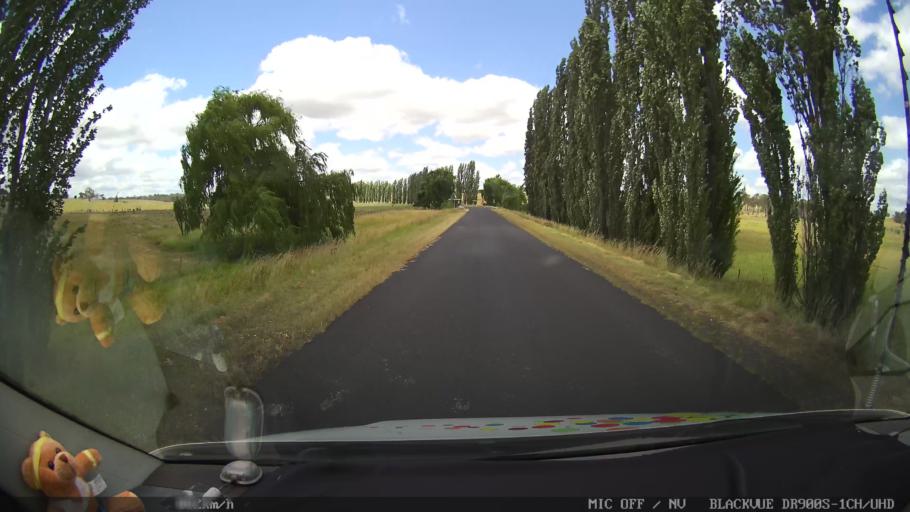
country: AU
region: New South Wales
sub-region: Glen Innes Severn
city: Glen Innes
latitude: -29.4342
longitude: 151.7551
